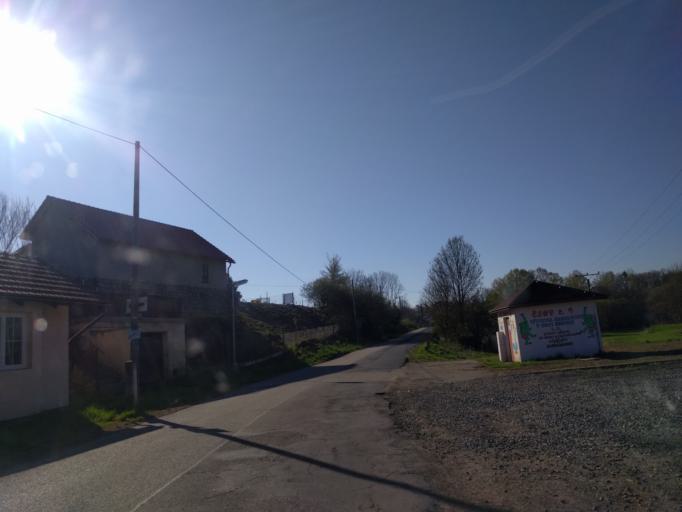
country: CZ
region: Central Bohemia
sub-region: Okres Praha-Vychod
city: Mnichovice
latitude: 49.9097
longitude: 14.7420
